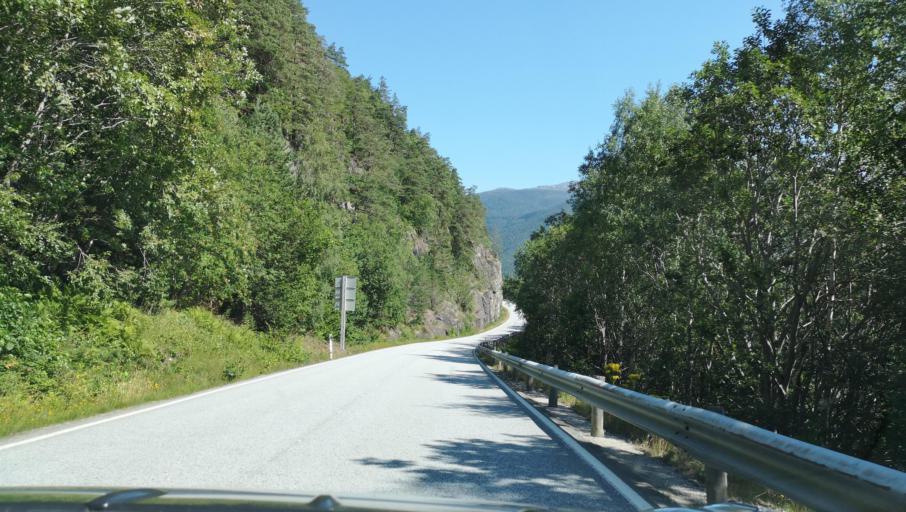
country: NO
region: Hordaland
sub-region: Ulvik
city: Ulvik
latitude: 60.4888
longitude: 6.8873
